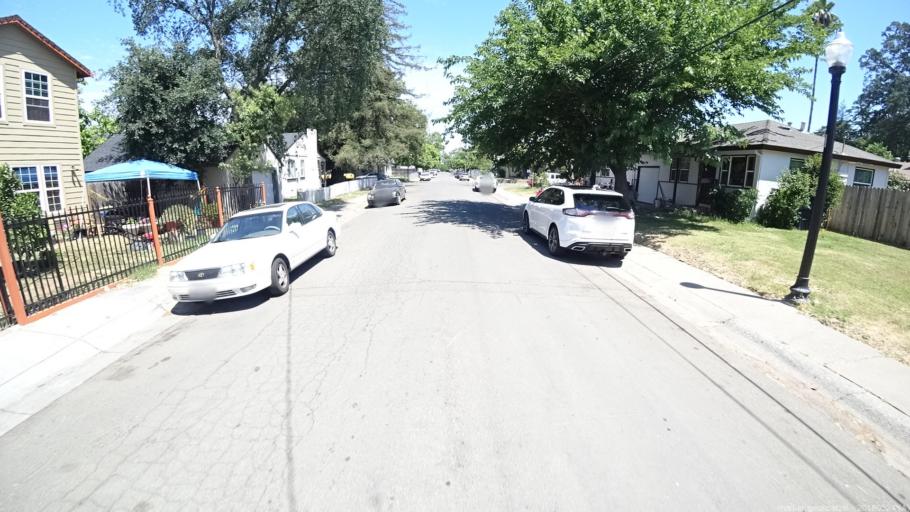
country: US
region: California
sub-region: Sacramento County
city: Sacramento
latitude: 38.6098
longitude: -121.4619
